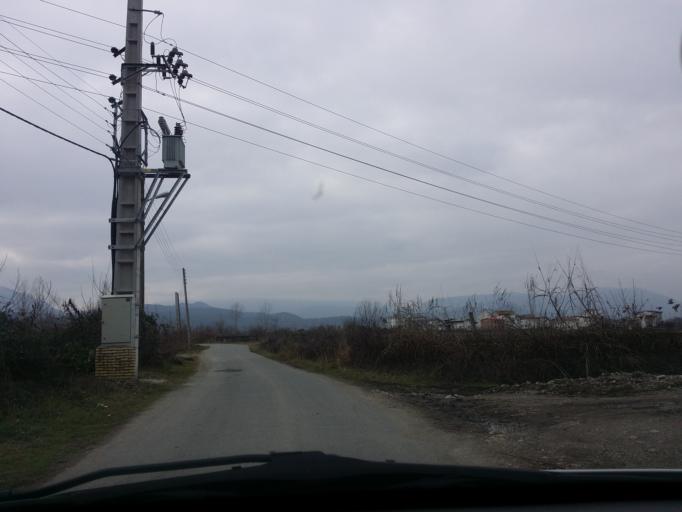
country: IR
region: Mazandaran
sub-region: Nowshahr
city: Nowshahr
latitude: 36.6530
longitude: 51.4744
